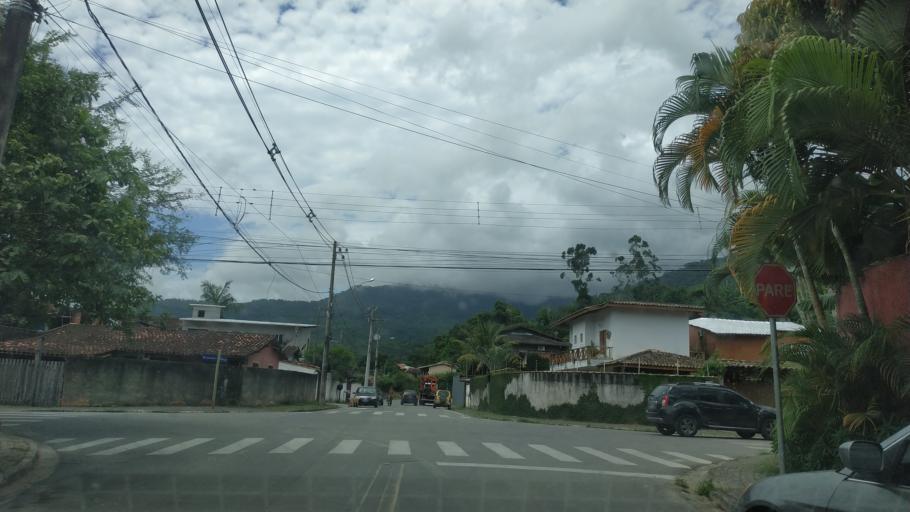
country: BR
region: Sao Paulo
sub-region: Ilhabela
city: Ilhabela
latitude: -23.8244
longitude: -45.3594
